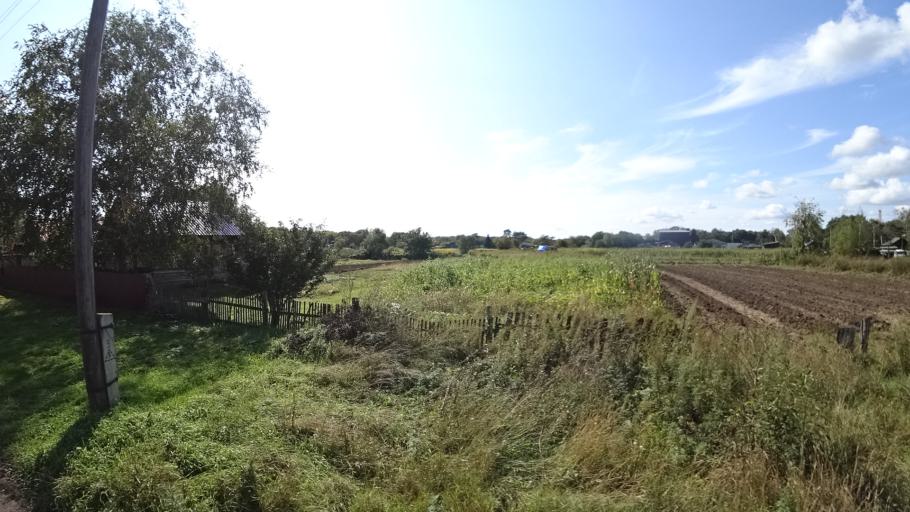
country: RU
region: Amur
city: Arkhara
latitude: 49.4018
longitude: 130.1447
